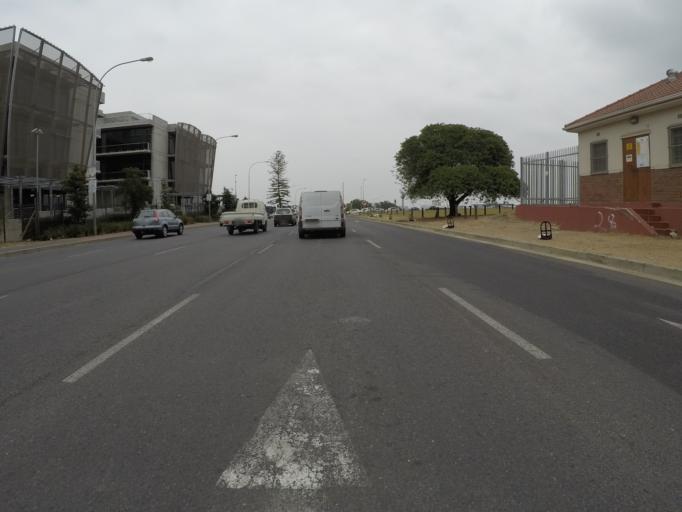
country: ZA
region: Western Cape
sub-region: City of Cape Town
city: Kraaifontein
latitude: -33.8852
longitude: 18.6354
